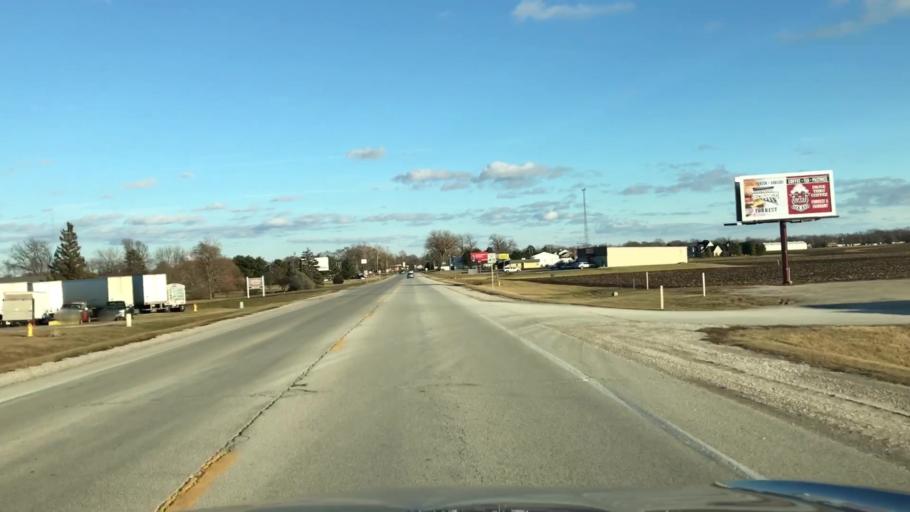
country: US
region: Illinois
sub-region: Livingston County
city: Fairbury
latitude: 40.7438
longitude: -88.5342
